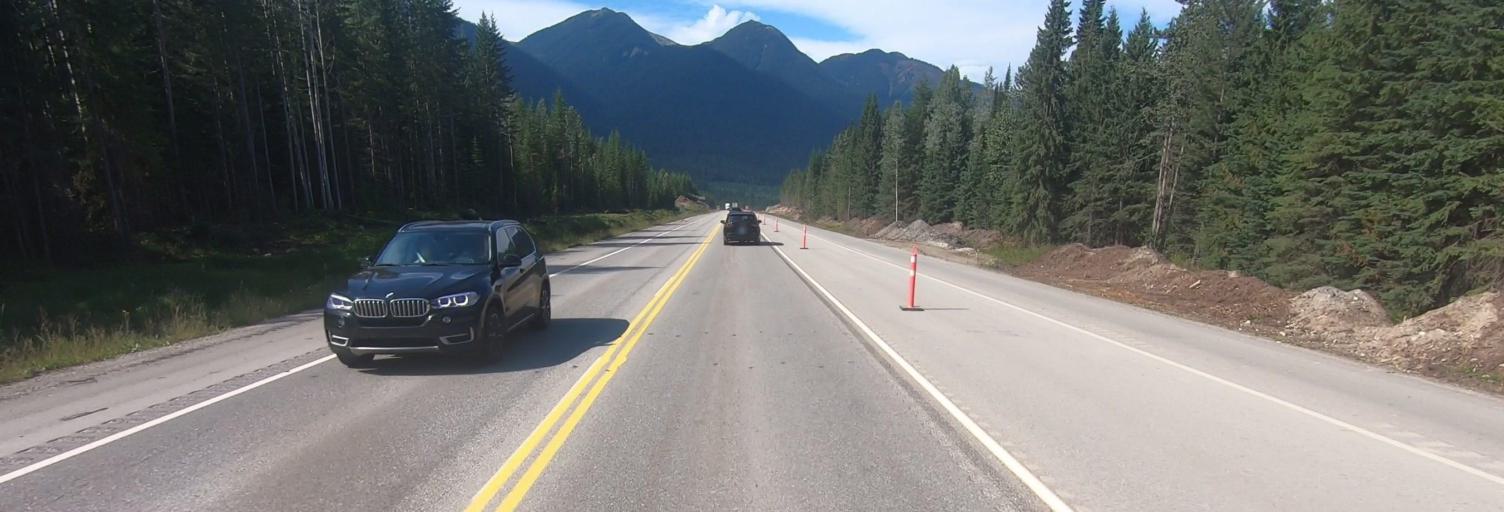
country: CA
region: British Columbia
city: Golden
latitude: 51.4821
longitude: -117.3431
